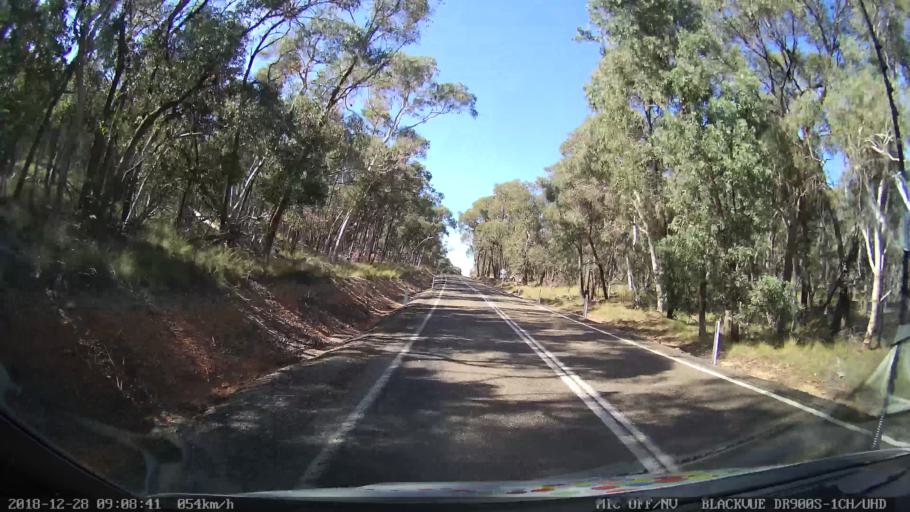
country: AU
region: New South Wales
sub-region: Upper Lachlan Shire
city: Crookwell
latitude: -34.2142
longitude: 149.3374
